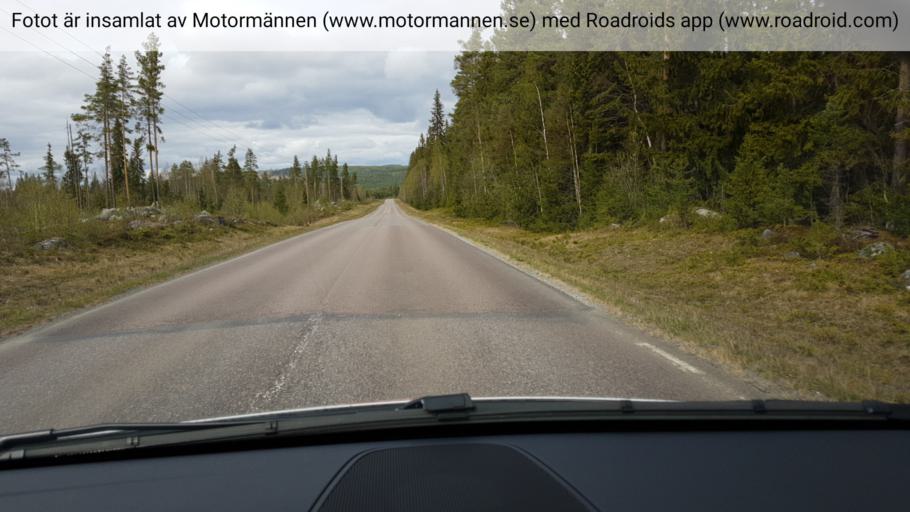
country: SE
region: Jaemtland
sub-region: Ragunda Kommun
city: Hammarstrand
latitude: 63.1980
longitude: 15.9427
